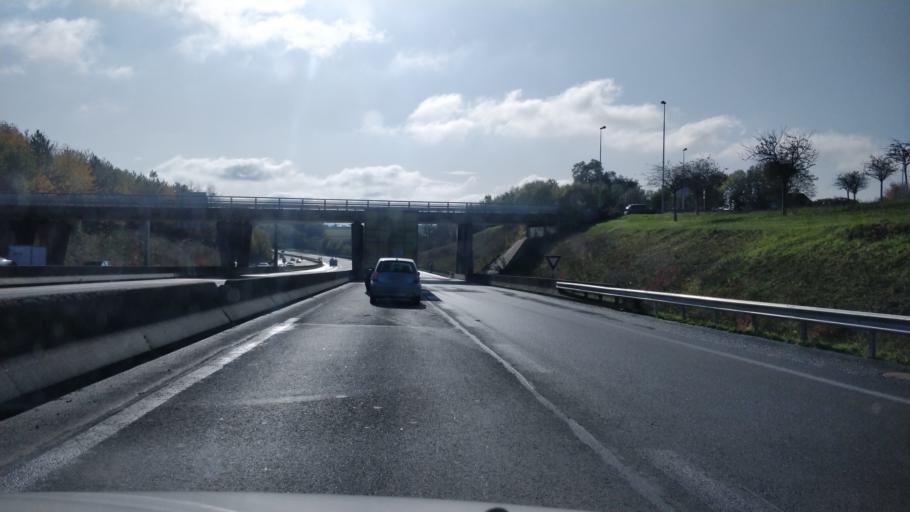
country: FR
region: Lower Normandy
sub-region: Departement du Calvados
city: Bretteville-sur-Odon
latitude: 49.1629
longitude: -0.4280
